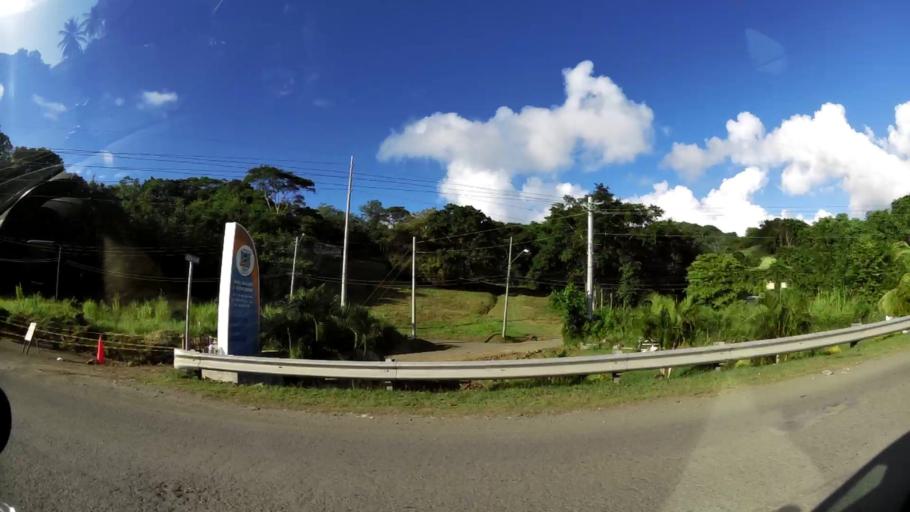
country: TT
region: Tobago
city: Scarborough
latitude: 11.1946
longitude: -60.6884
